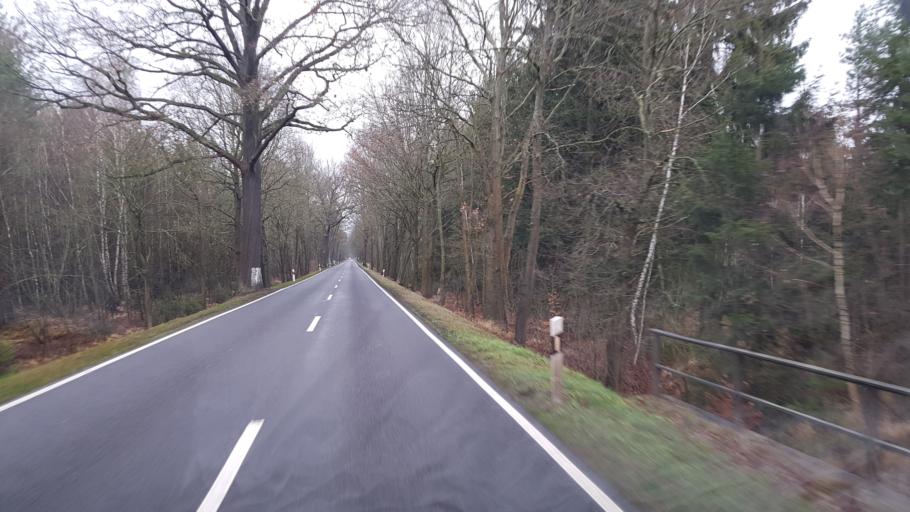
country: DE
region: Brandenburg
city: Altdobern
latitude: 51.7082
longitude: 14.0221
